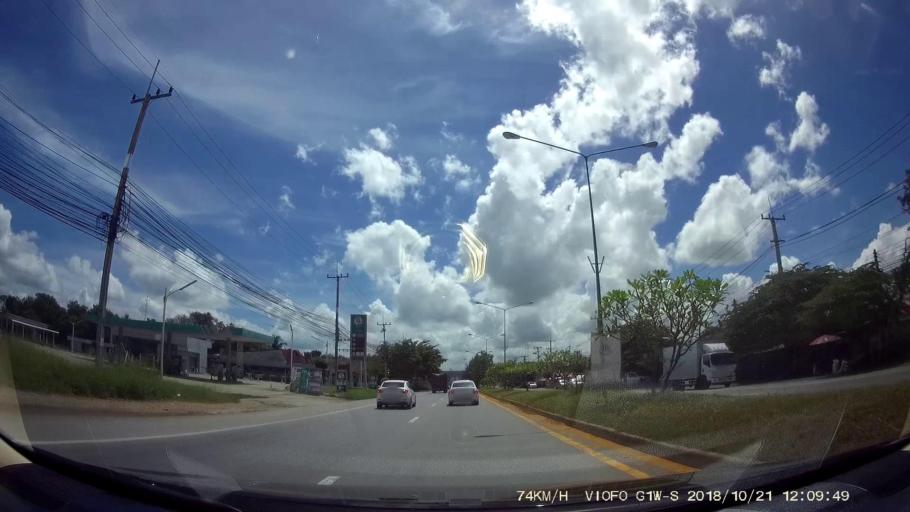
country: TH
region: Chaiyaphum
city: Chatturat
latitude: 15.4166
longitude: 101.8332
